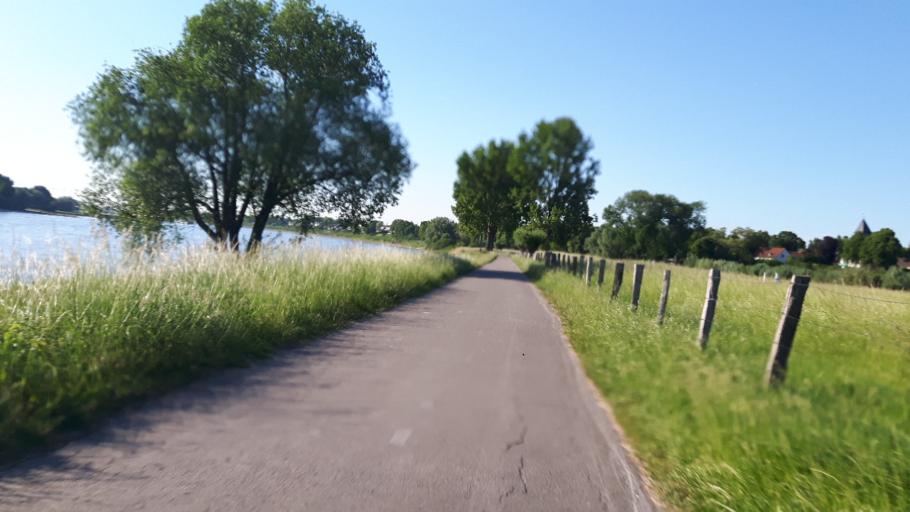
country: DE
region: North Rhine-Westphalia
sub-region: Regierungsbezirk Dusseldorf
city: Meerbusch
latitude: 51.3175
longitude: 6.7370
